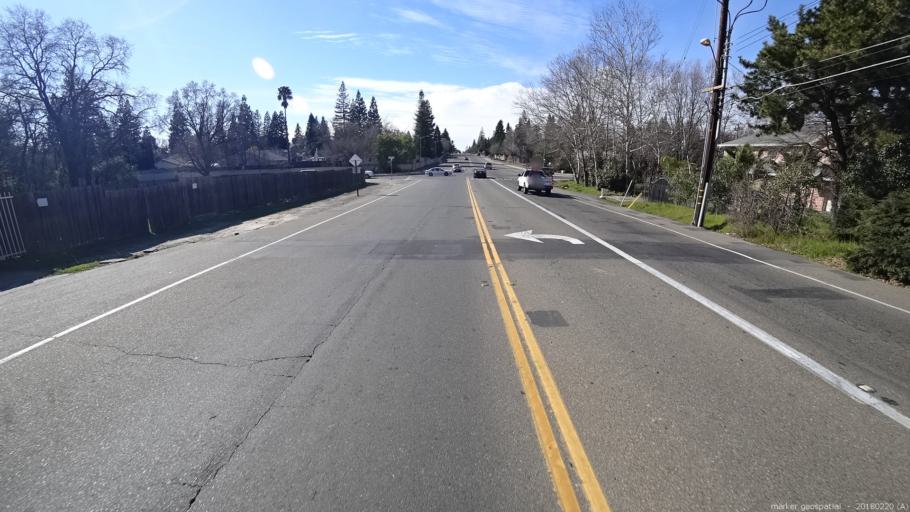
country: US
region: California
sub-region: Sacramento County
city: Orangevale
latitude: 38.7004
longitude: -121.2435
